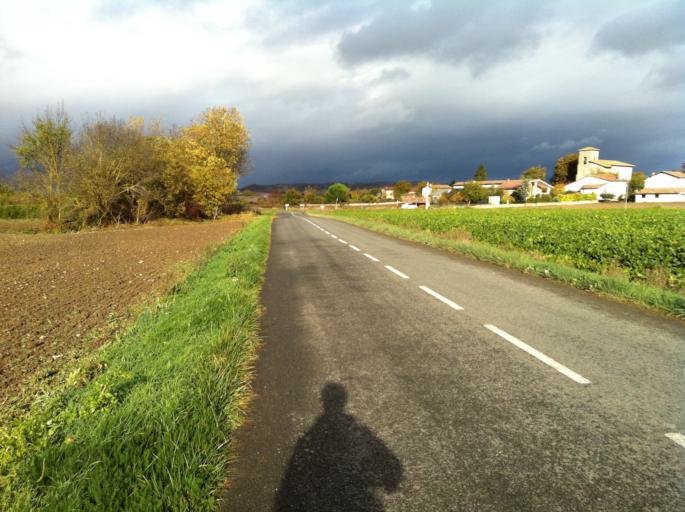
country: ES
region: Basque Country
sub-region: Provincia de Alava
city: Gasteiz / Vitoria
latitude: 42.8717
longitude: -2.7151
